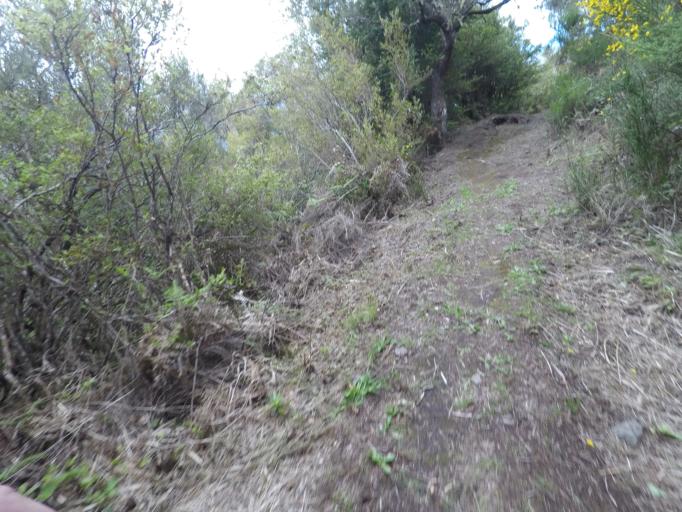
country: PT
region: Madeira
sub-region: Camara de Lobos
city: Curral das Freiras
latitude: 32.7688
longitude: -16.9748
